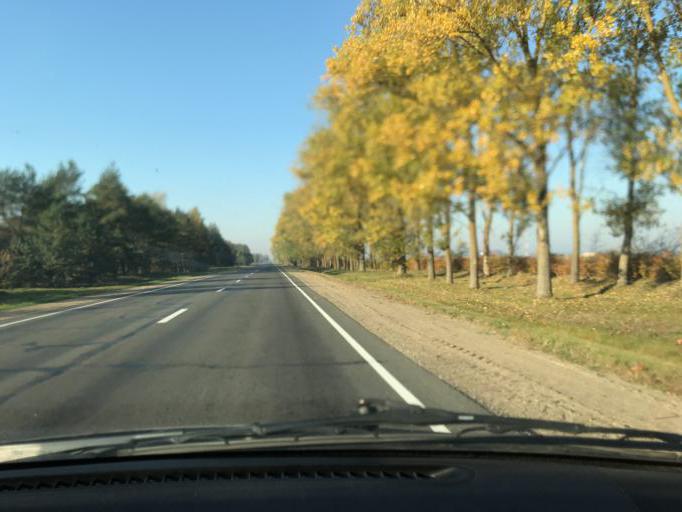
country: BY
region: Brest
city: Baranovichi
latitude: 52.9007
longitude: 25.8739
